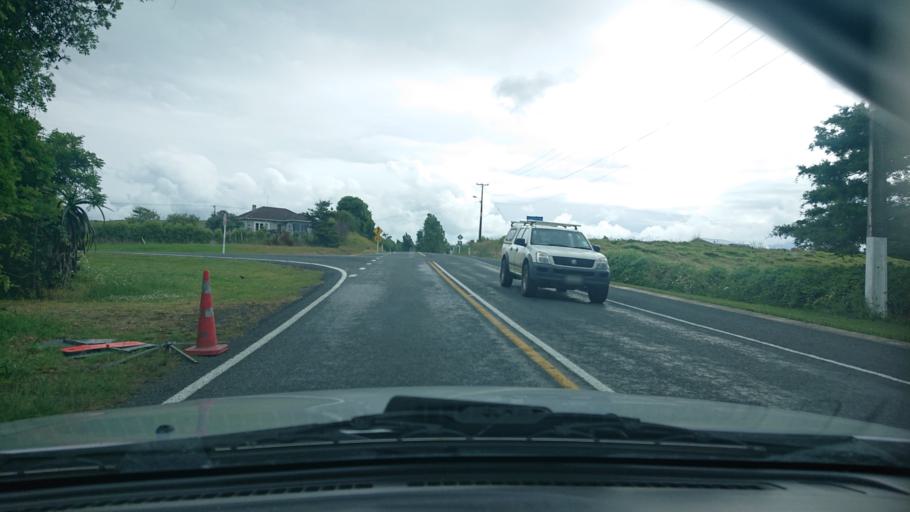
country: NZ
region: Auckland
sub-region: Auckland
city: Wellsford
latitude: -36.3771
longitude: 174.4525
